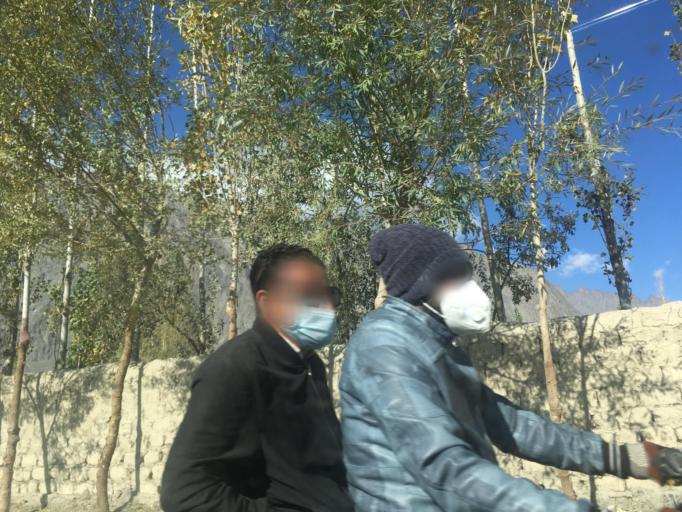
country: PK
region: Gilgit-Baltistan
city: Skardu
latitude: 35.3468
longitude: 75.5206
